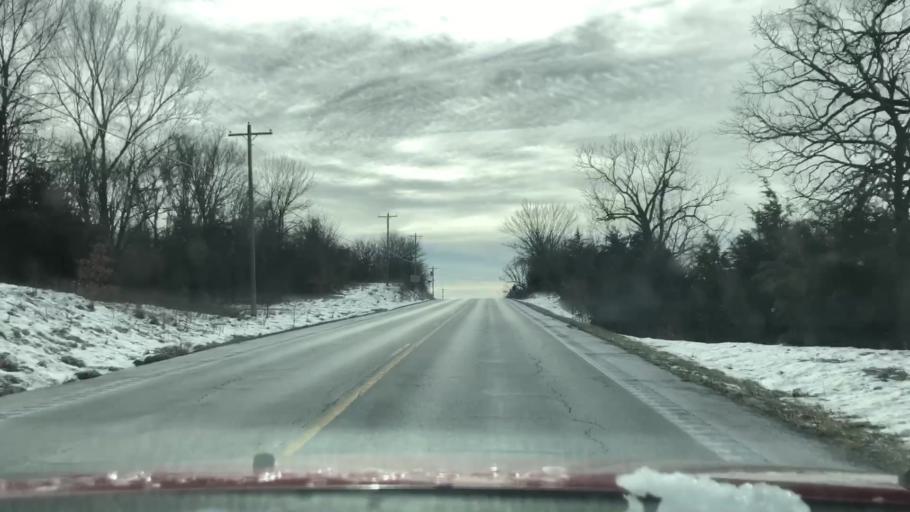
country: US
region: Missouri
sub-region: Jackson County
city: Oak Grove
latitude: 38.9700
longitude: -94.1308
